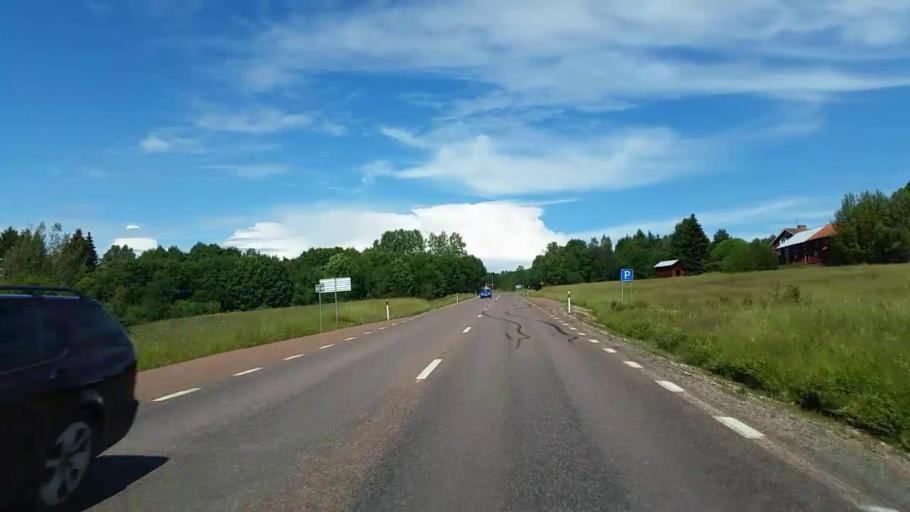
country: SE
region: Dalarna
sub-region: Rattviks Kommun
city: Raettvik
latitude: 61.0006
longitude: 15.2186
